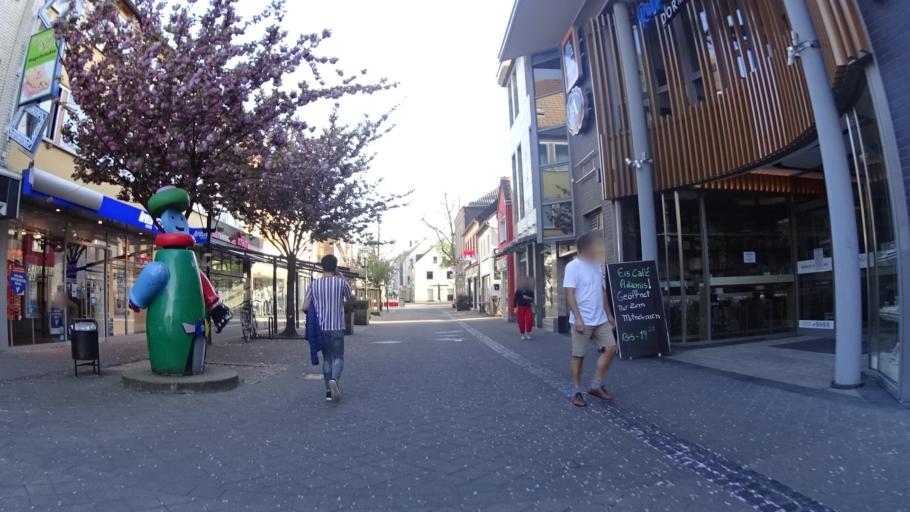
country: DE
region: North Rhine-Westphalia
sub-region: Regierungsbezirk Dusseldorf
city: Dormagen
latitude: 51.0942
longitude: 6.8412
